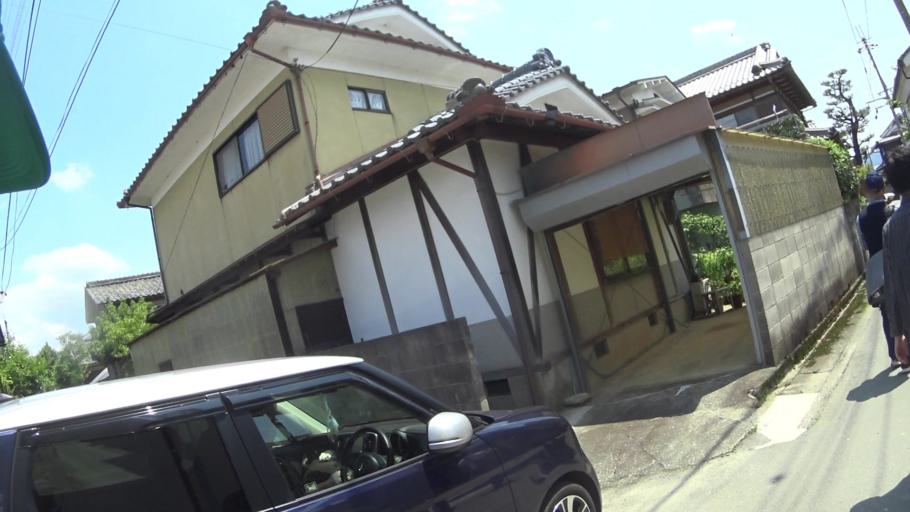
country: JP
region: Kyoto
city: Kameoka
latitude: 35.0324
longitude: 135.5718
